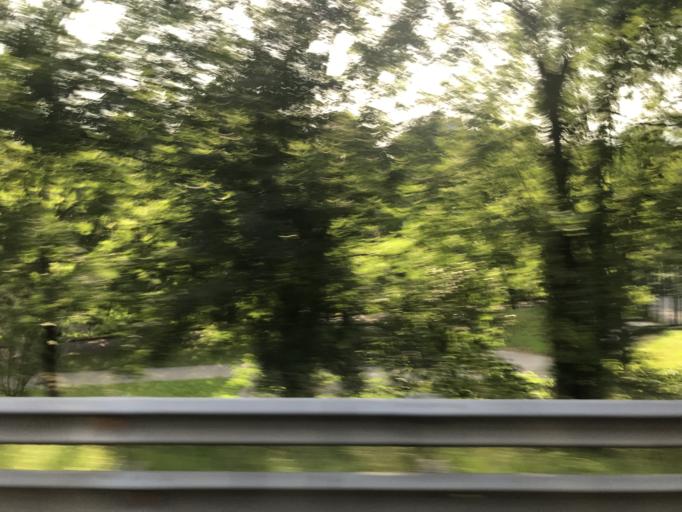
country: ES
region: Basque Country
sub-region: Provincia de Guipuzcoa
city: Andoain
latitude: 43.2188
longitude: -2.0247
